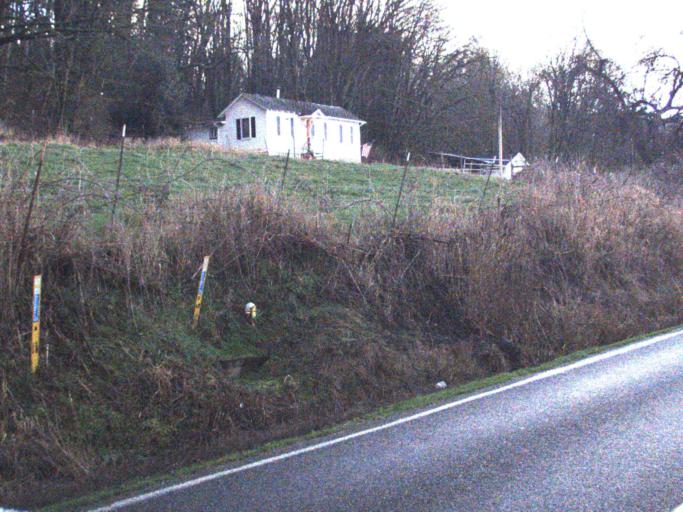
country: US
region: Washington
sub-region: Snohomish County
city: Silver Firs
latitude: 47.8886
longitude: -122.1393
